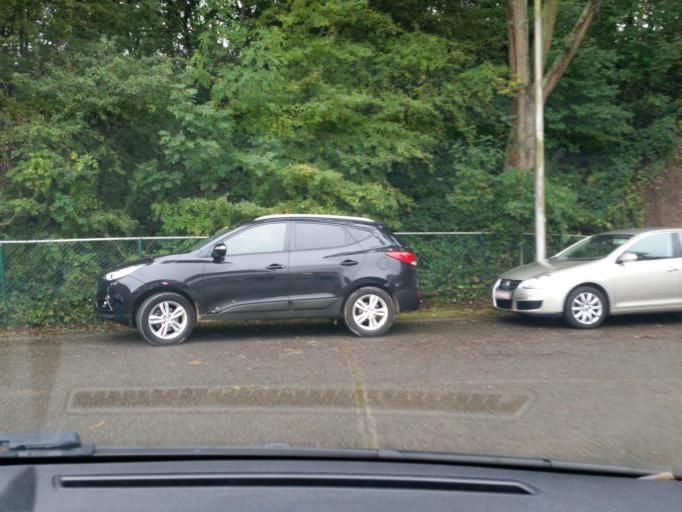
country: BE
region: Flanders
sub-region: Provincie Antwerpen
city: Hoboken
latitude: 51.1647
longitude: 4.3465
